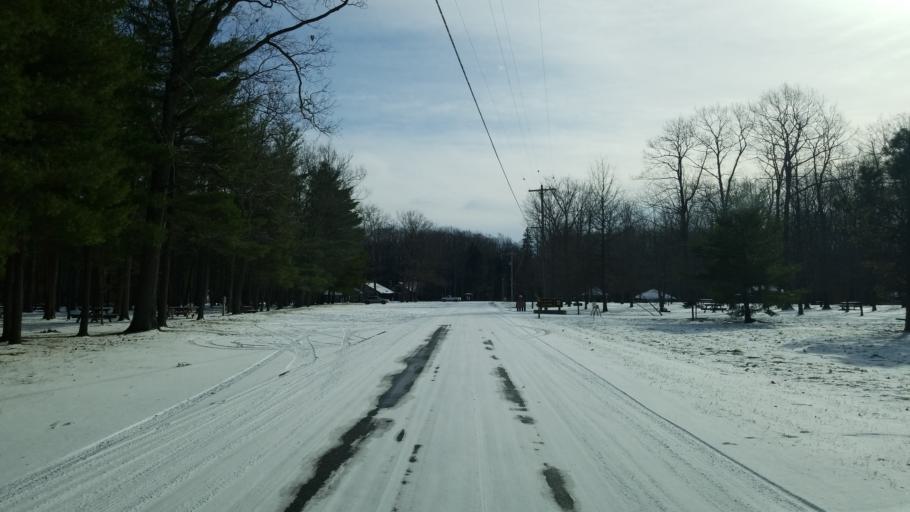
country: US
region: Pennsylvania
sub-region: Clearfield County
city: Clearfield
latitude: 41.1144
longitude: -78.5271
